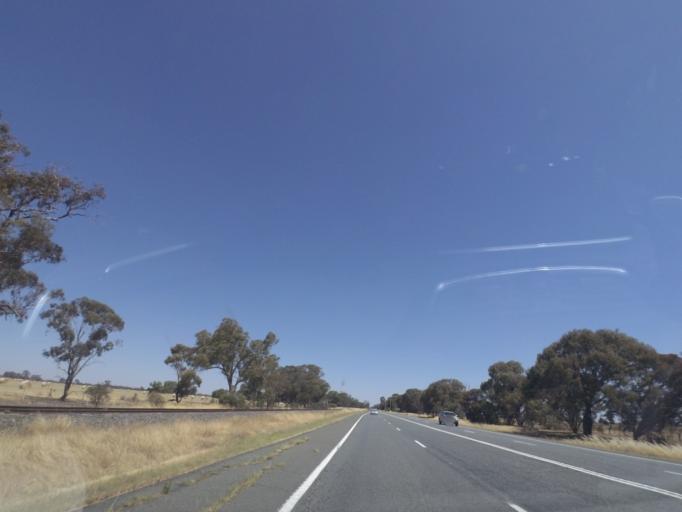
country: AU
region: Victoria
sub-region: Greater Shepparton
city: Shepparton
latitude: -36.1940
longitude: 145.4319
